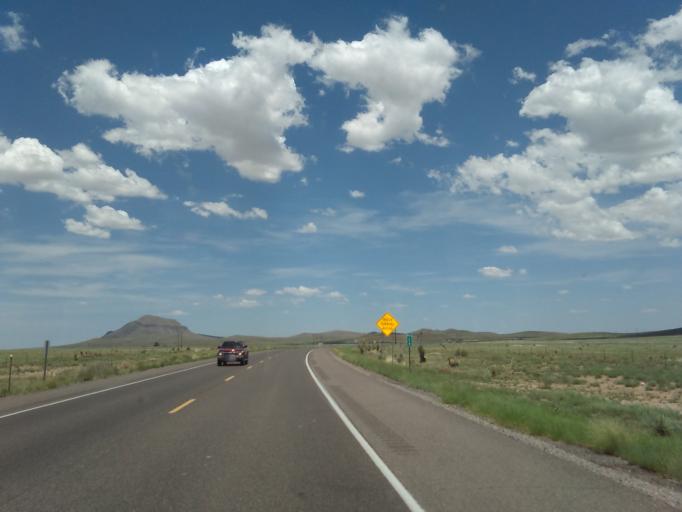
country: US
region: New Mexico
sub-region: Dona Ana County
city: Hatch
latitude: 32.5579
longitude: -107.4723
